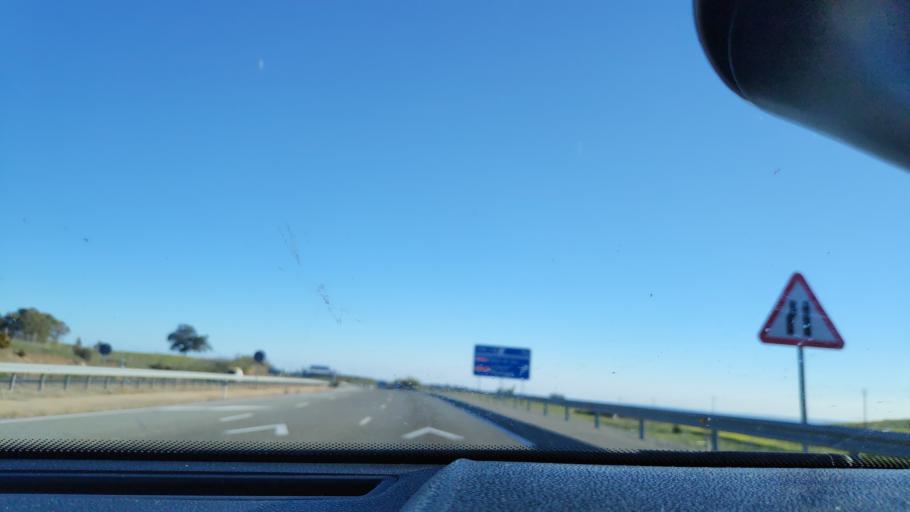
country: ES
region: Andalusia
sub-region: Provincia de Sevilla
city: El Ronquillo
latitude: 37.6370
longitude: -6.1533
